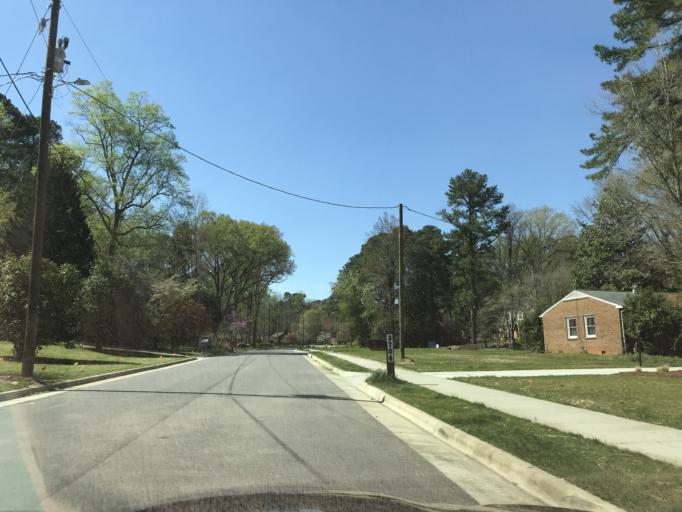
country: US
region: North Carolina
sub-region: Wake County
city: West Raleigh
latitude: 35.7699
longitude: -78.7048
